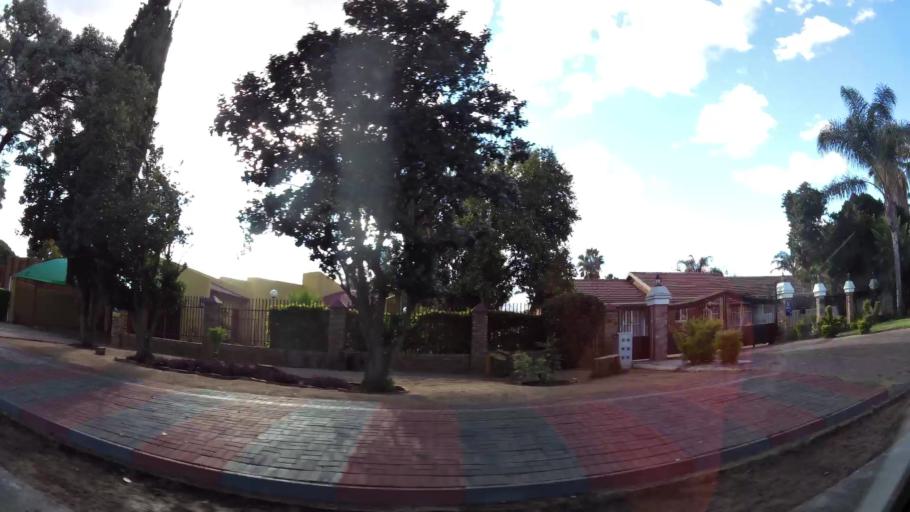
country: ZA
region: Limpopo
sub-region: Capricorn District Municipality
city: Polokwane
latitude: -23.9060
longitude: 29.4952
